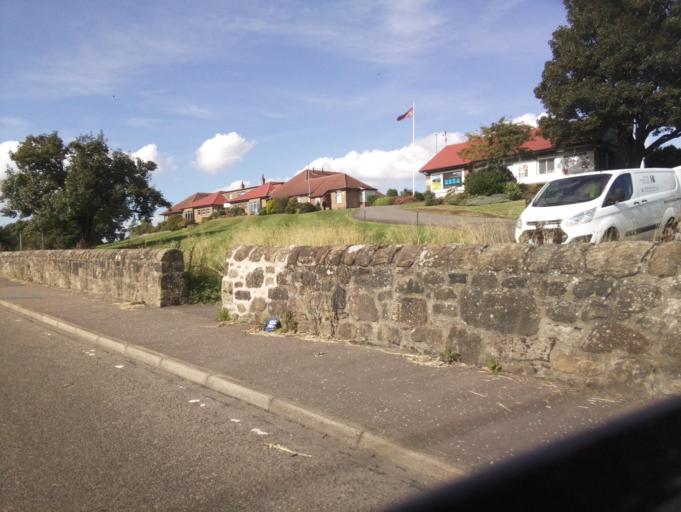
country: GB
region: Scotland
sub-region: Falkirk
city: Larbert
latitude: 56.0339
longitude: -3.8524
